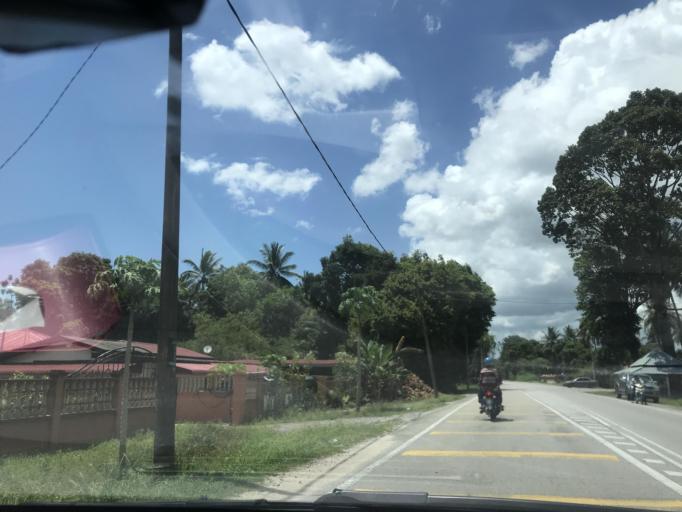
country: MY
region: Kelantan
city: Tumpat
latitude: 6.1792
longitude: 102.1794
